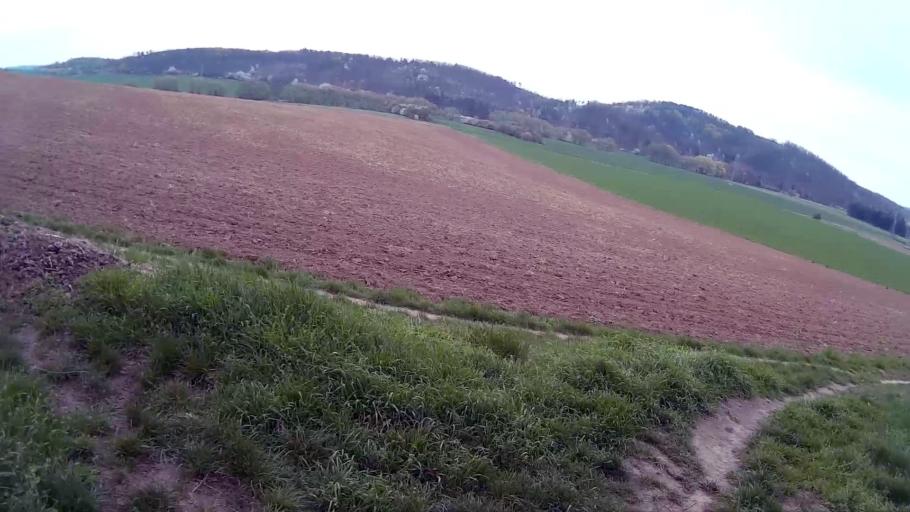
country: CZ
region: South Moravian
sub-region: Mesto Brno
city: Mokra Hora
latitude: 49.2307
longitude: 16.5538
